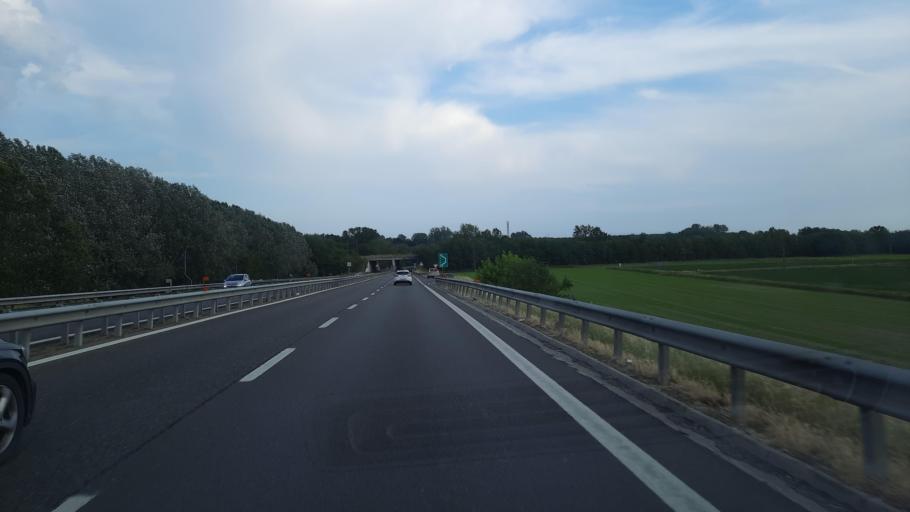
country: IT
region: Lombardy
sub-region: Provincia di Pavia
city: San Martino Siccomario
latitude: 45.1787
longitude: 9.1259
